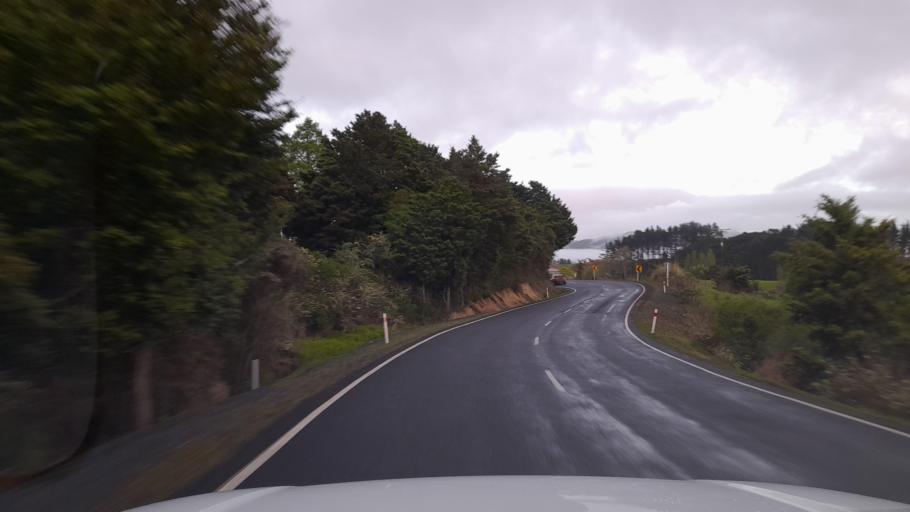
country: NZ
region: Northland
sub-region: Whangarei
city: Maungatapere
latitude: -35.7052
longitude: 174.0153
